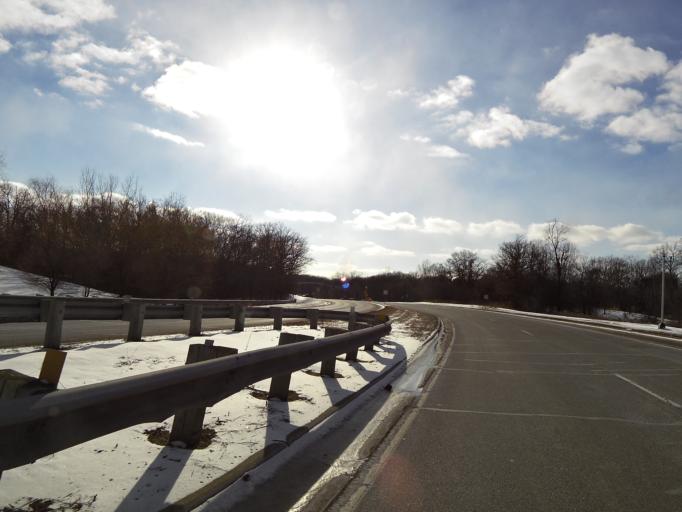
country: US
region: Minnesota
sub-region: Dakota County
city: Apple Valley
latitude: 44.7598
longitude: -93.2207
